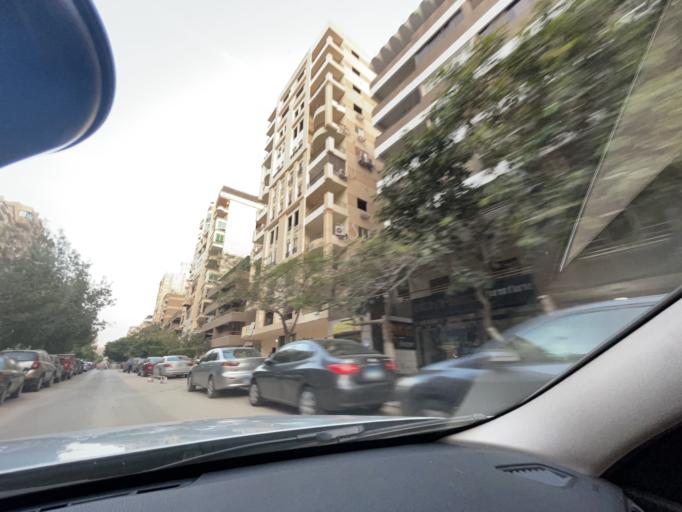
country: EG
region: Muhafazat al Qahirah
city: Cairo
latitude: 30.0597
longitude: 31.3481
